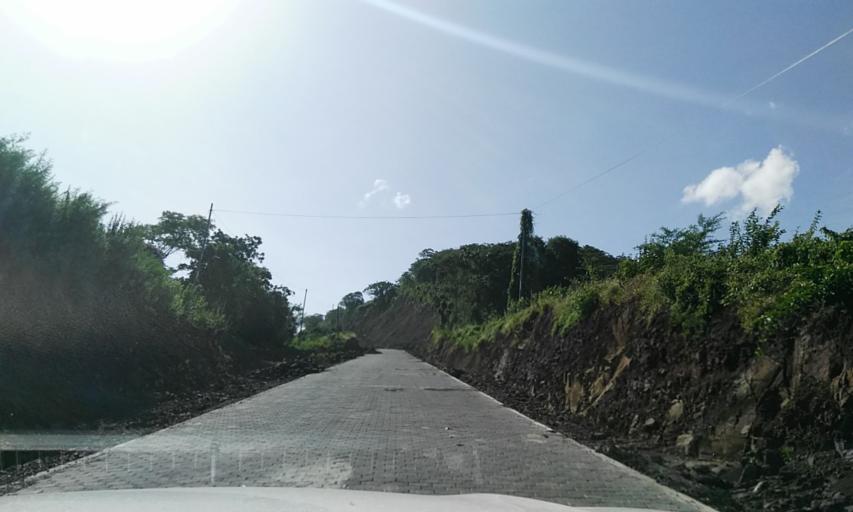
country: NI
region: Matagalpa
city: Terrabona
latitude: 12.7549
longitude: -85.9854
